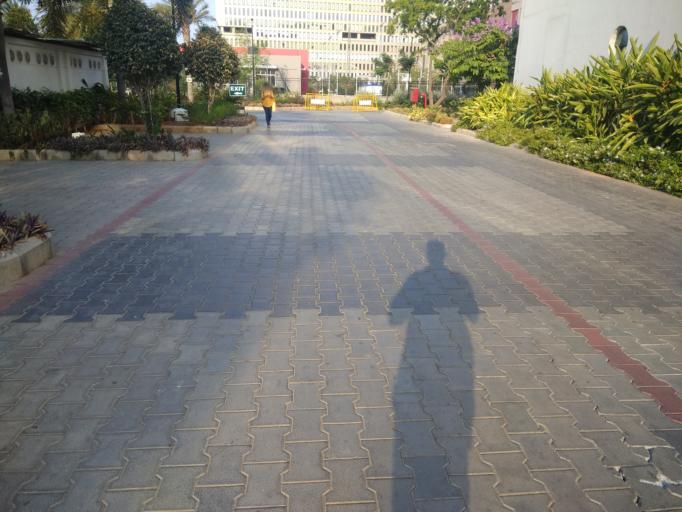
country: IN
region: Tamil Nadu
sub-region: Chennai
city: Gandhi Nagar
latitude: 12.9915
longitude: 80.2433
